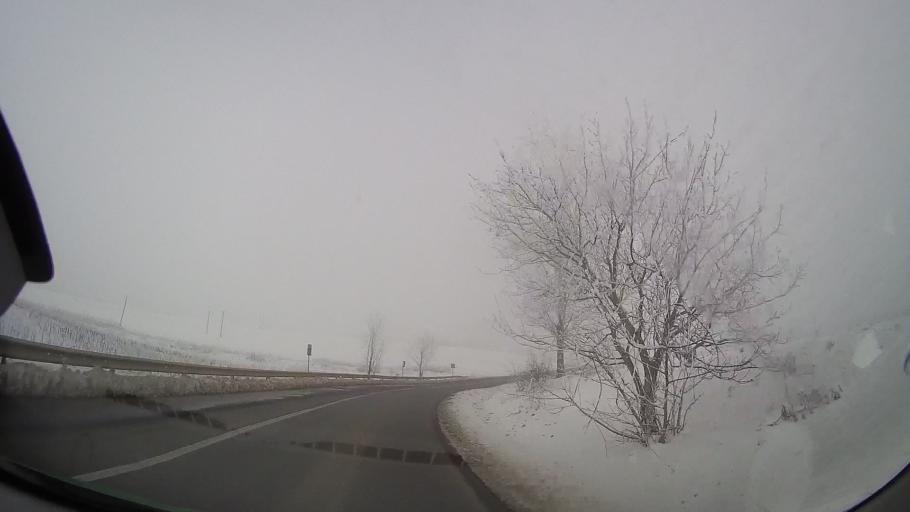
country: RO
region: Iasi
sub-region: Comuna Stolniceni-Prajescu
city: Stolniceni-Prajescu
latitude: 47.1883
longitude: 26.7366
